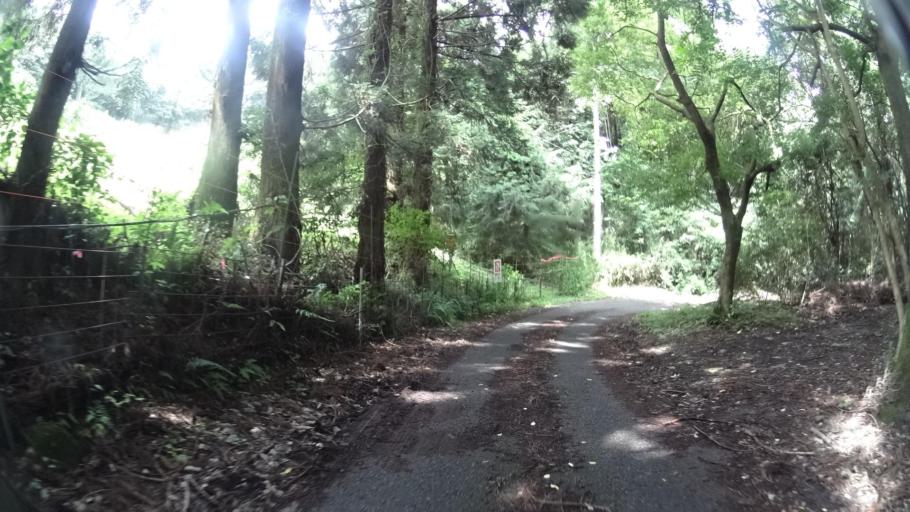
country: JP
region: Kyoto
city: Maizuru
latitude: 35.5307
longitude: 135.3417
